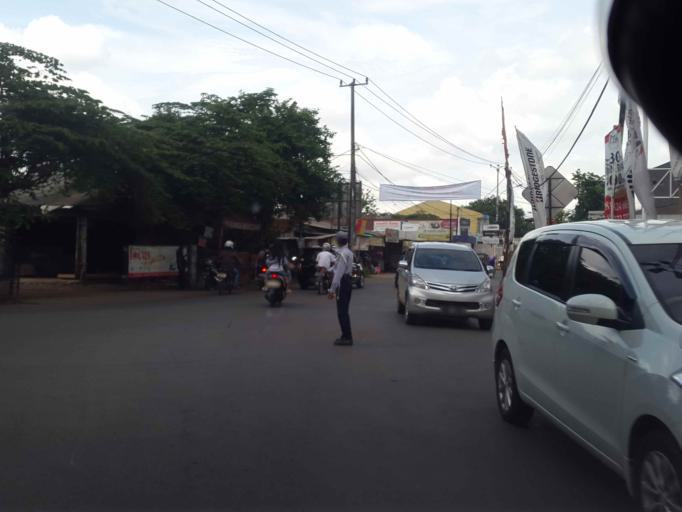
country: ID
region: West Java
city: Bekasi
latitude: -6.3083
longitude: 106.9552
